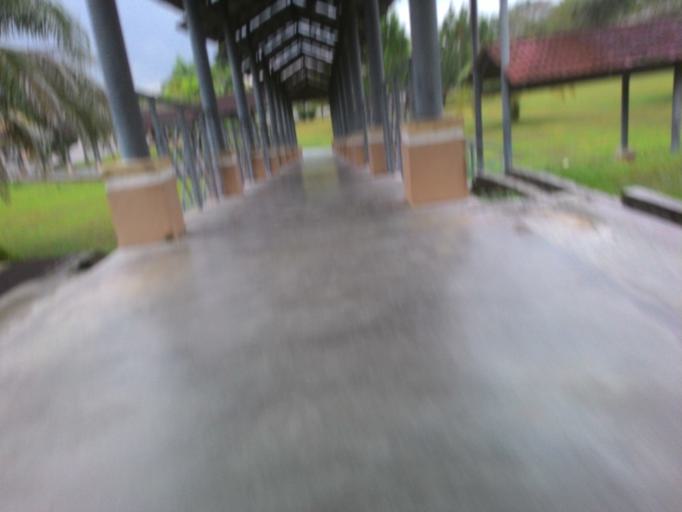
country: MY
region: Kedah
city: Kulim
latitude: 5.3825
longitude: 100.5794
